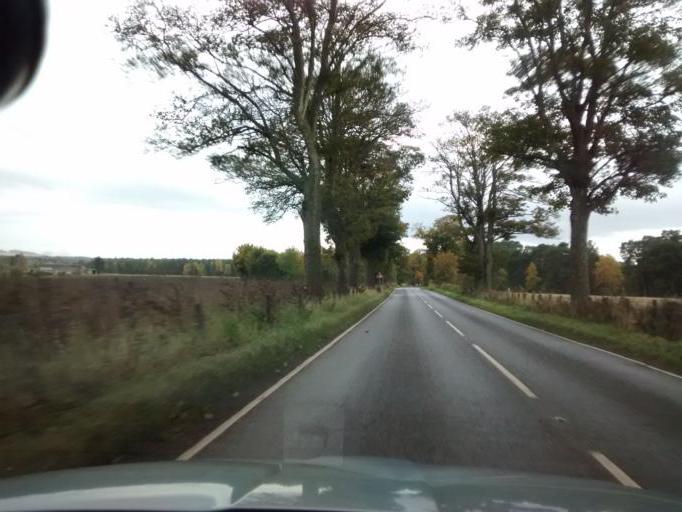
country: GB
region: Scotland
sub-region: Perth and Kinross
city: Blairgowrie
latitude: 56.5536
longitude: -3.3496
